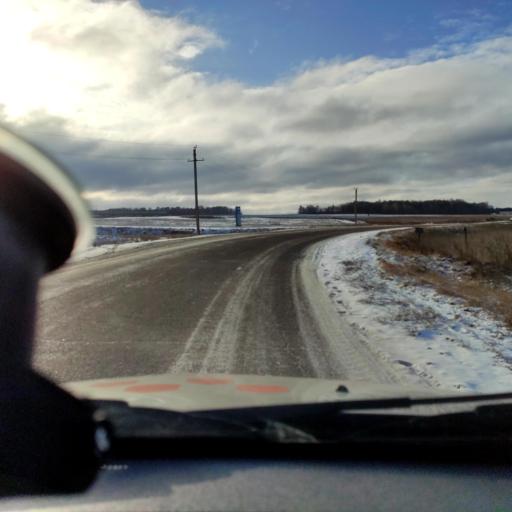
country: RU
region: Bashkortostan
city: Mikhaylovka
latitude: 54.7986
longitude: 55.7799
